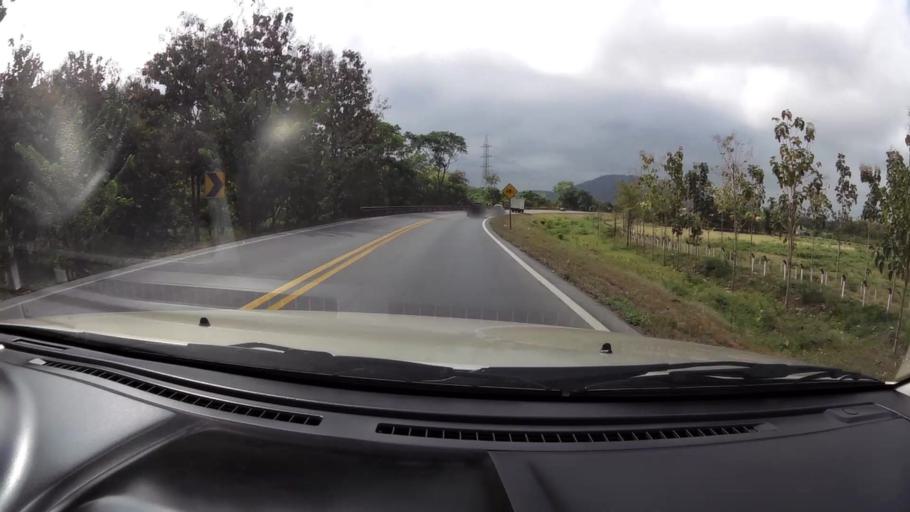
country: EC
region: Guayas
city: Naranjal
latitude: -2.4084
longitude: -79.6240
